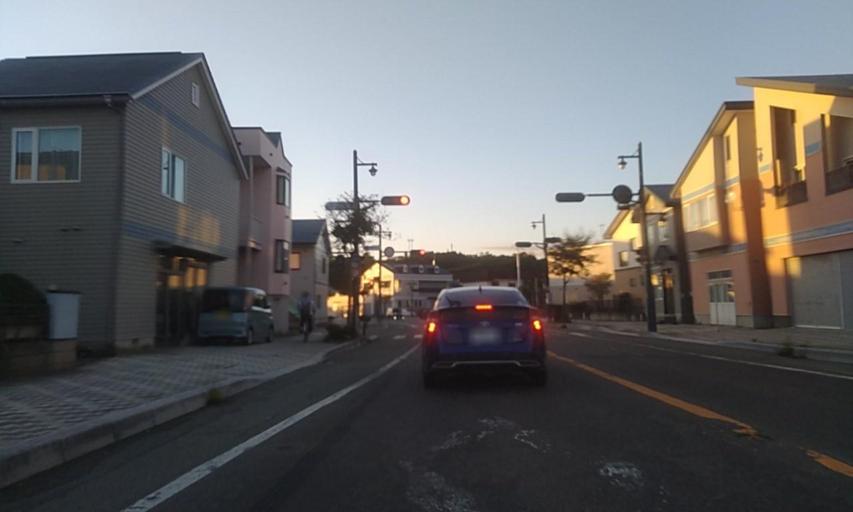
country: JP
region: Hokkaido
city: Shizunai-furukawacho
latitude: 42.1595
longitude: 142.7815
